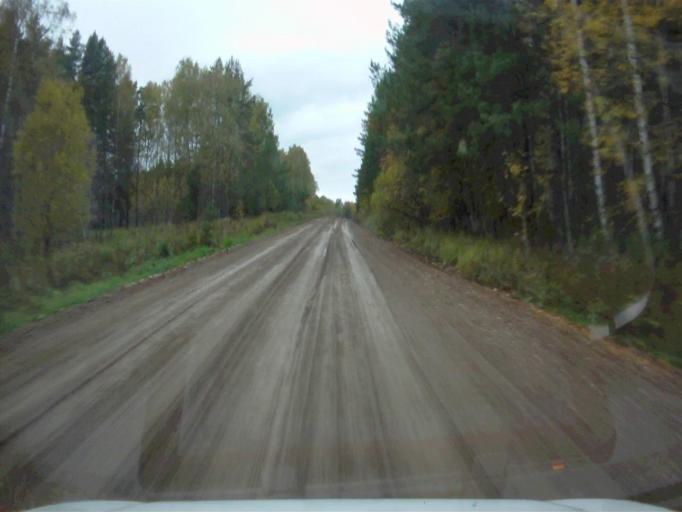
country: RU
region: Chelyabinsk
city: Nyazepetrovsk
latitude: 56.0977
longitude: 59.3955
